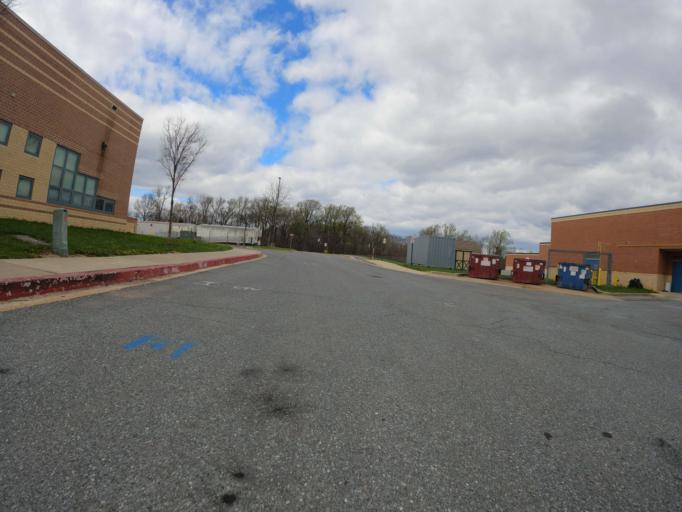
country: US
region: Maryland
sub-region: Howard County
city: North Laurel
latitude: 39.1451
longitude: -76.8587
